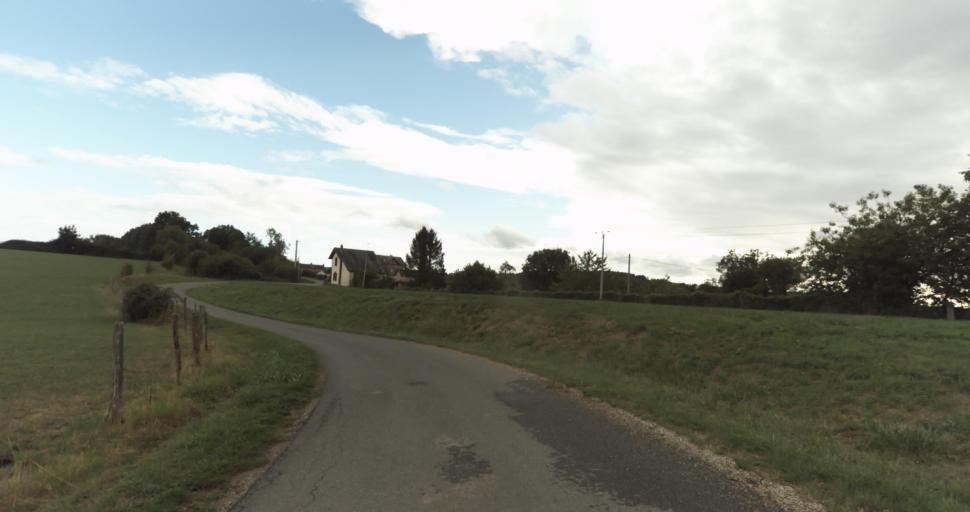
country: FR
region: Lower Normandy
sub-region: Departement de l'Orne
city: Sainte-Gauburge-Sainte-Colombe
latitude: 48.7292
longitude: 0.3951
